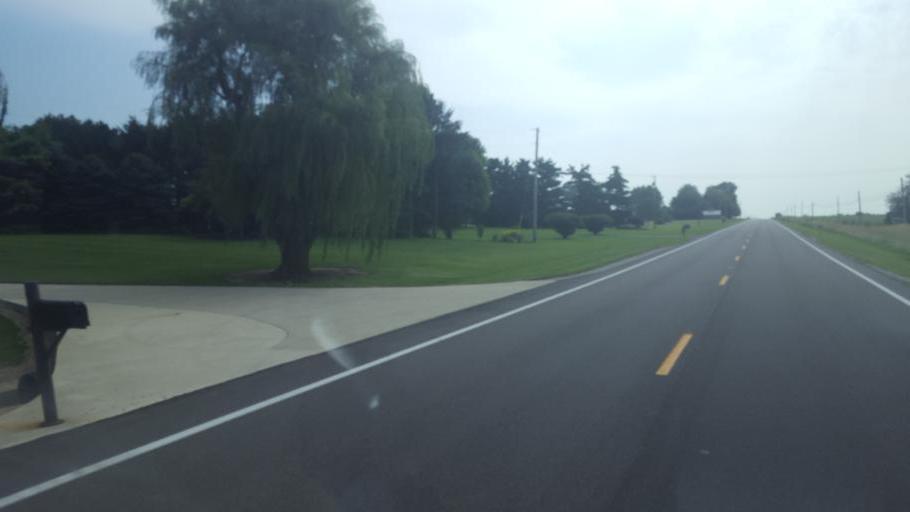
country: US
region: Ohio
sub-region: Hardin County
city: Kenton
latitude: 40.6440
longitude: -83.5548
